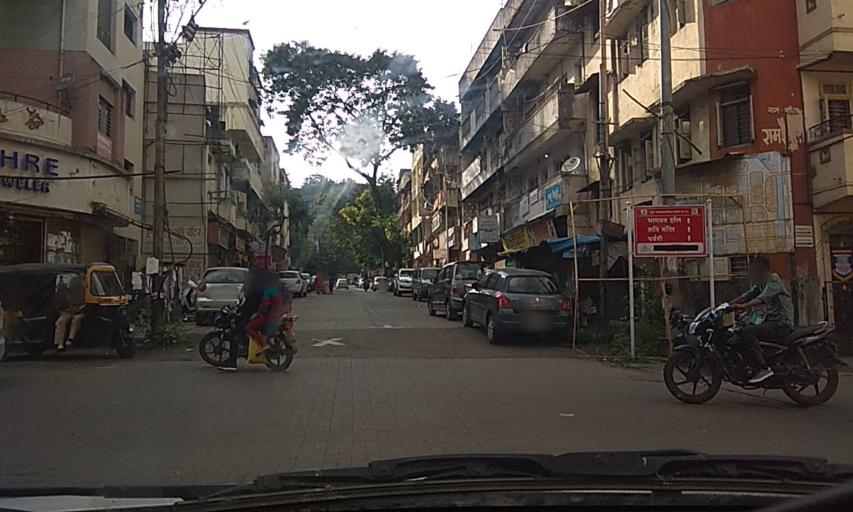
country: IN
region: Maharashtra
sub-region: Pune Division
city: Pune
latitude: 18.4975
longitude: 73.8511
